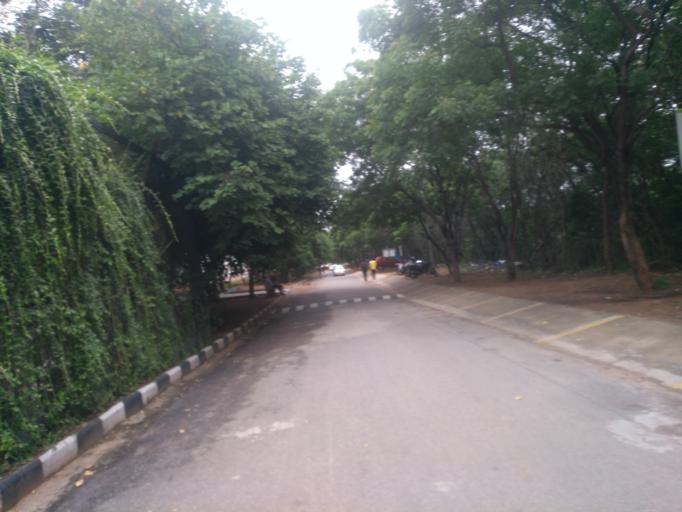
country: IN
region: Telangana
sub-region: Medak
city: Serilingampalle
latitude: 17.4455
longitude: 78.3484
